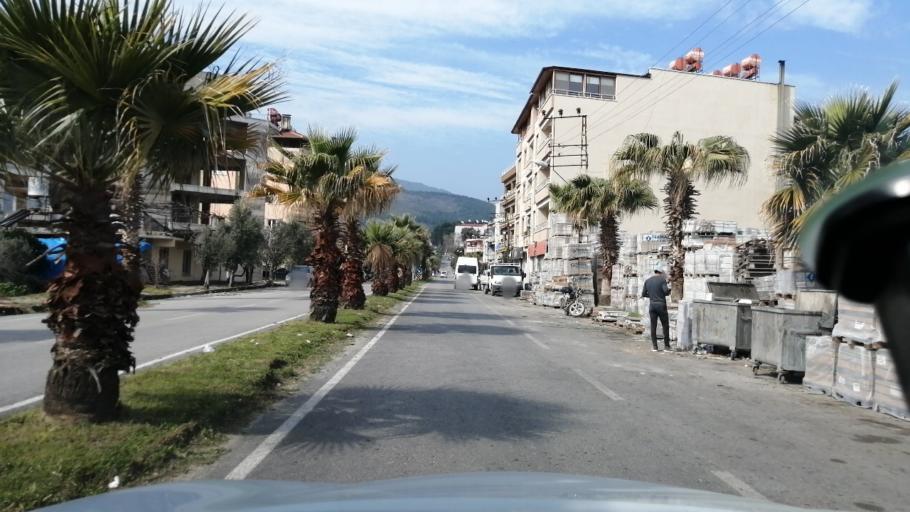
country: TR
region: Hatay
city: Serinyol
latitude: 36.3521
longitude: 36.2119
